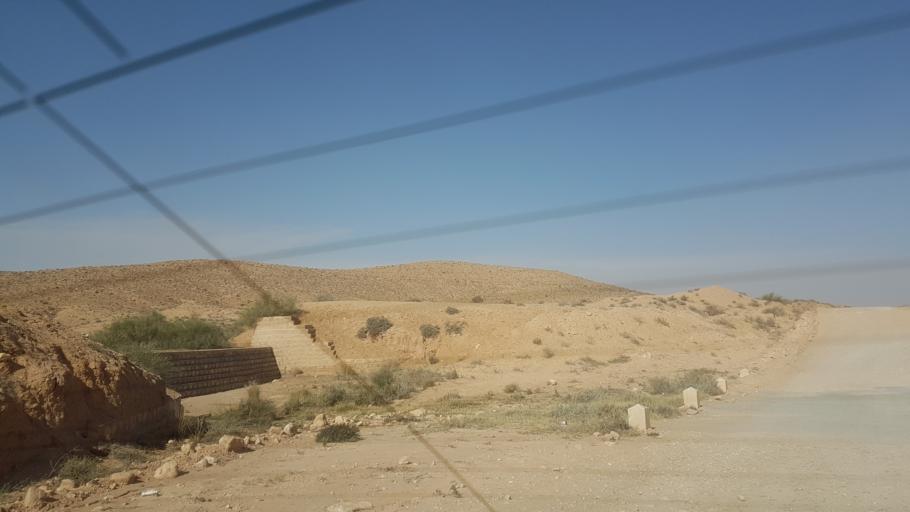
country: TN
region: Qabis
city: Matmata
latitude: 33.6434
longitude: 9.7372
